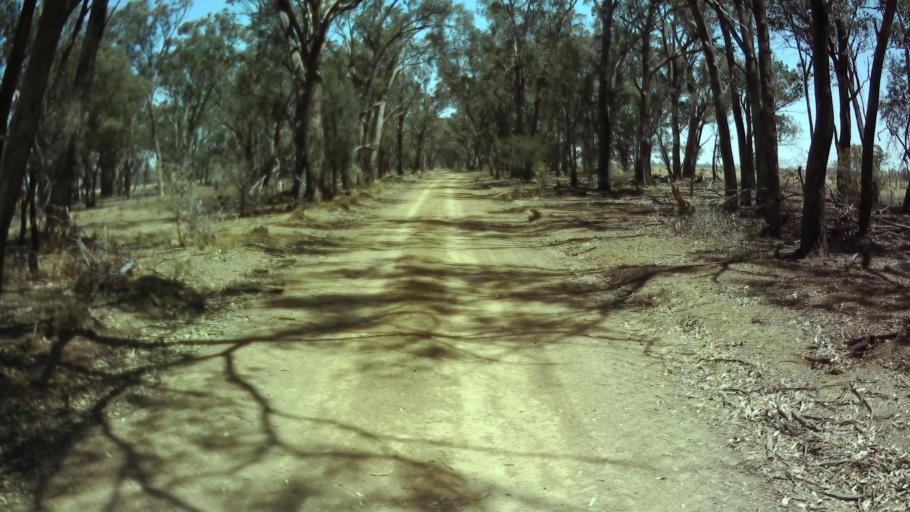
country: AU
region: New South Wales
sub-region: Weddin
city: Grenfell
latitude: -34.0484
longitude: 147.8329
